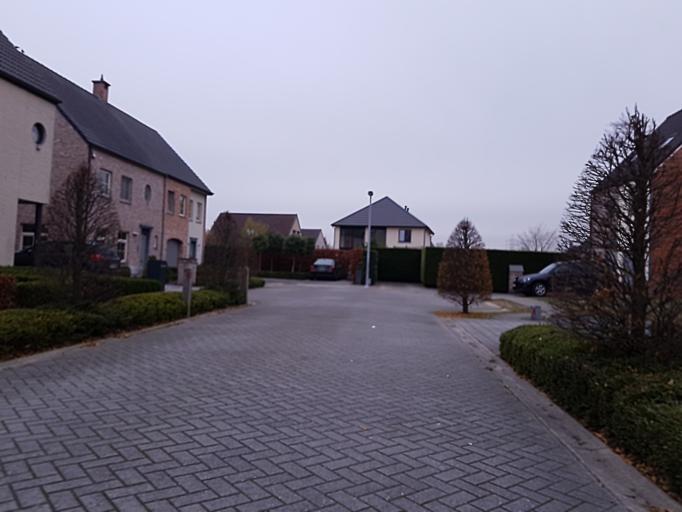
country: BE
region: Flanders
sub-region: Provincie Antwerpen
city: Rumst
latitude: 51.0333
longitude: 4.4148
